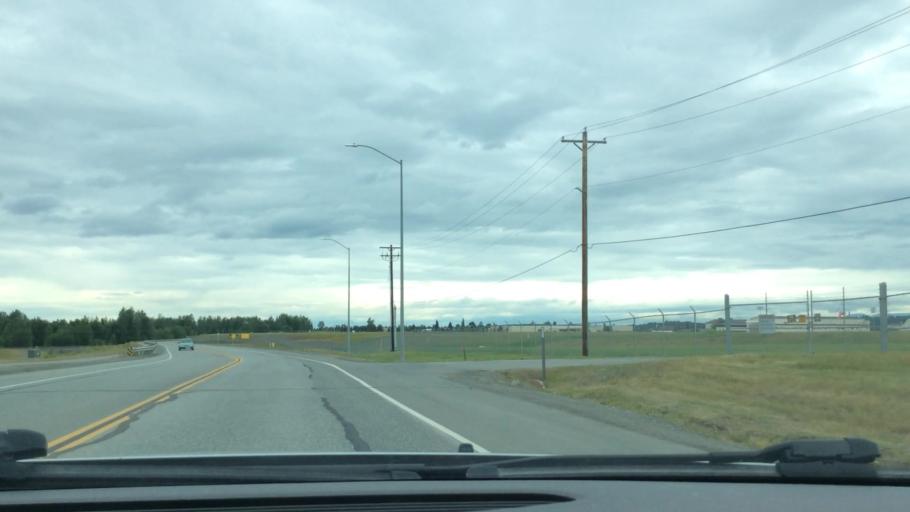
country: US
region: Alaska
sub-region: Anchorage Municipality
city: Anchorage
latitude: 61.2404
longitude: -149.7865
